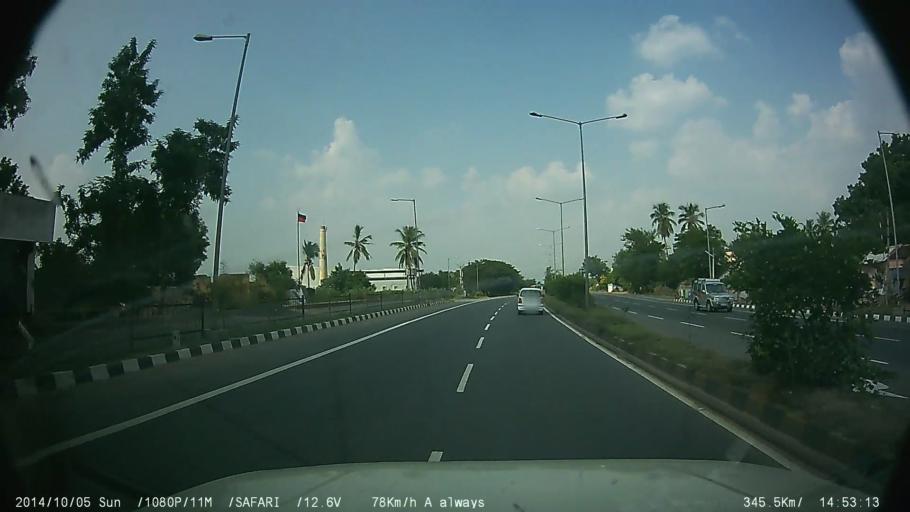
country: IN
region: Tamil Nadu
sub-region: Kancheepuram
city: Madurantakam
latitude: 12.5338
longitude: 79.9011
